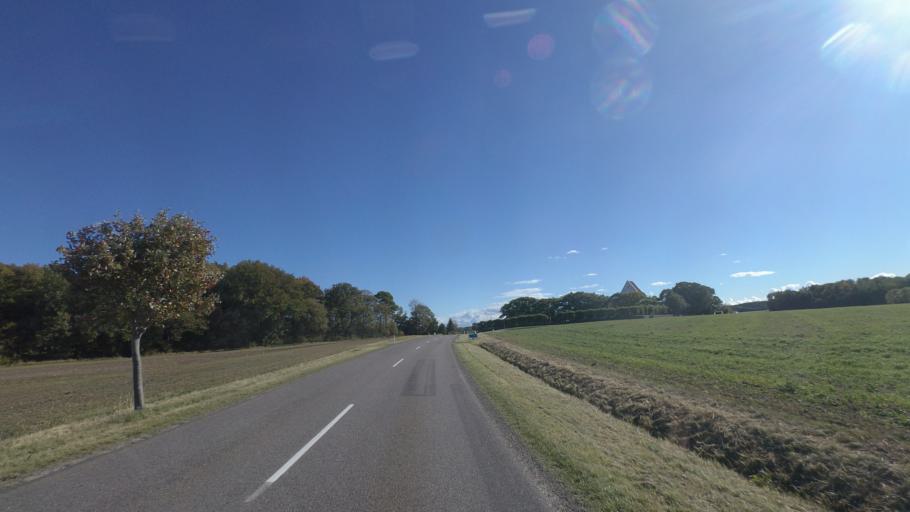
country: DK
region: Capital Region
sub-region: Bornholm Kommune
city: Nexo
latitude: 55.1192
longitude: 15.1042
